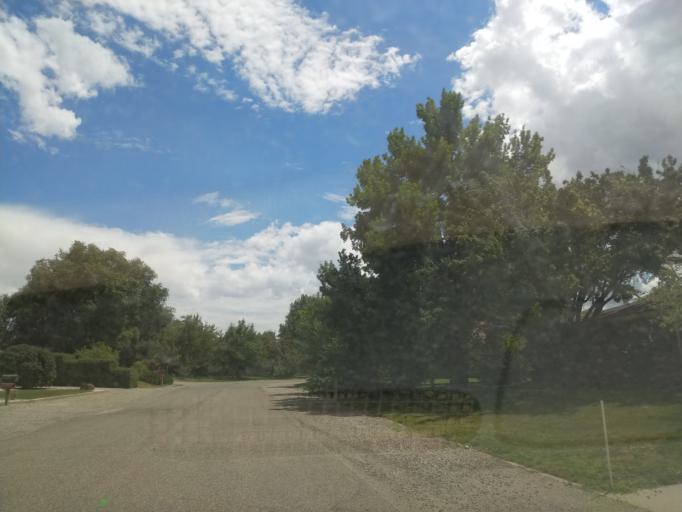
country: US
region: Colorado
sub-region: Mesa County
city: Redlands
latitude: 39.0691
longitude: -108.6485
